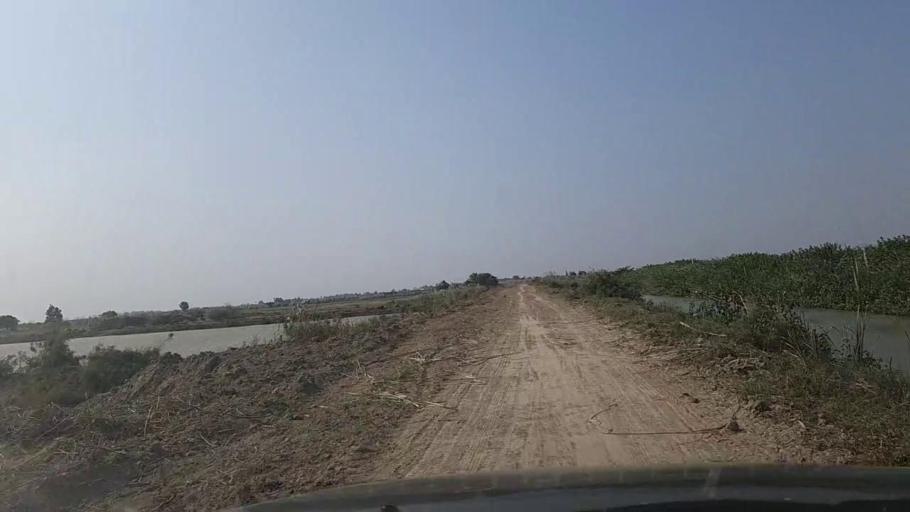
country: PK
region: Sindh
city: Gharo
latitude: 24.7165
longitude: 67.6595
